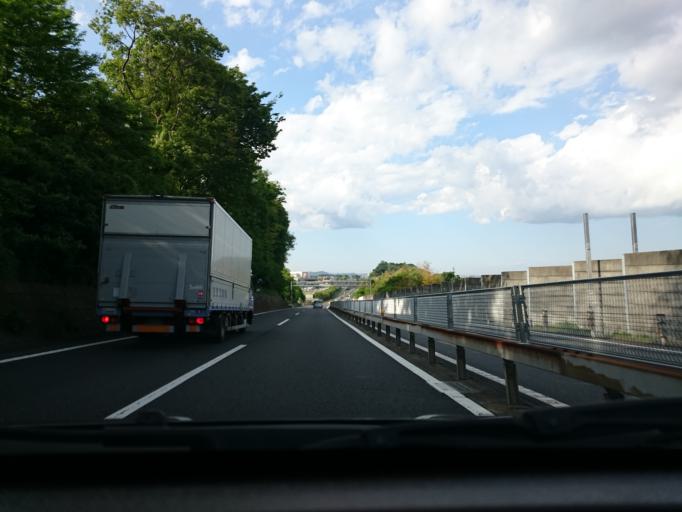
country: JP
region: Kanagawa
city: Oiso
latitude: 35.3451
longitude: 139.2969
